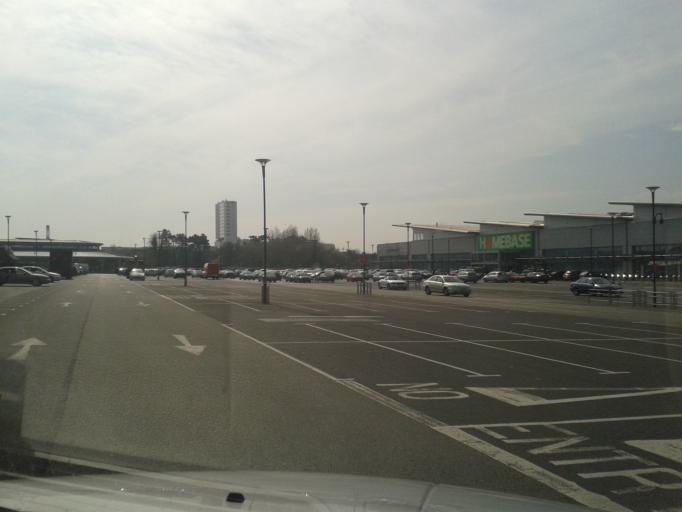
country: IE
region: Leinster
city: Ballymun
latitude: 53.4056
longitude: -6.2598
